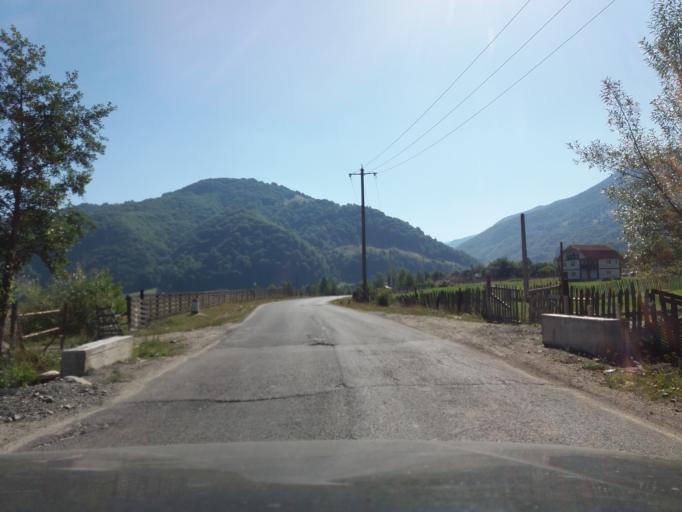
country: RO
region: Hunedoara
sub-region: Oras Petrila
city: Petrila
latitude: 45.4206
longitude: 23.4209
